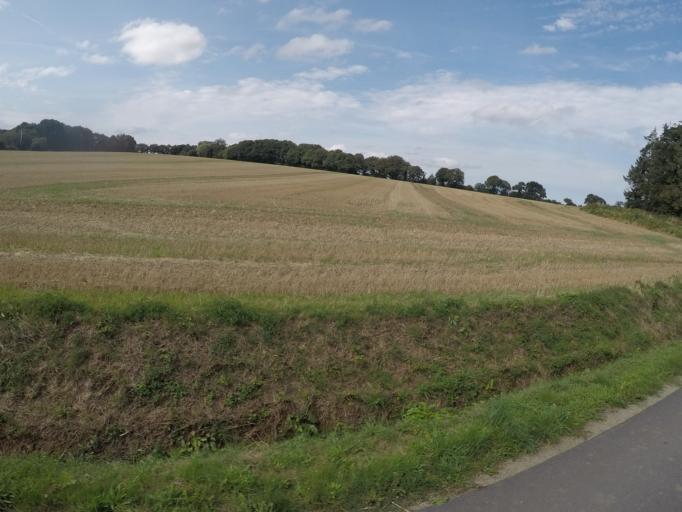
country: FR
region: Brittany
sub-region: Departement des Cotes-d'Armor
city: Goudelin
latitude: 48.5980
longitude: -2.9985
